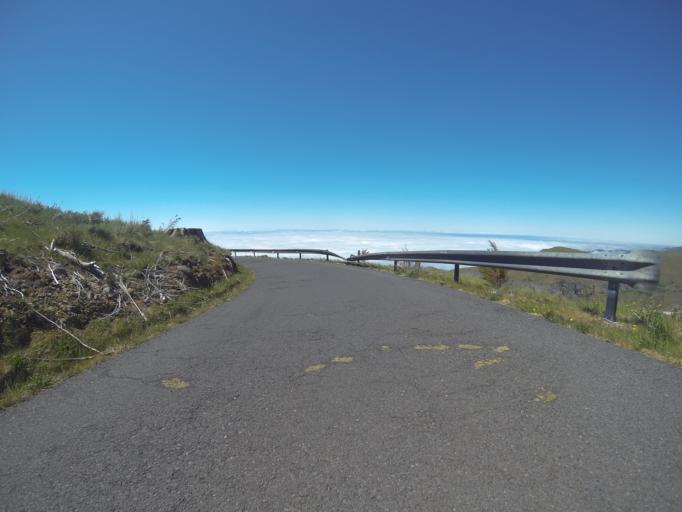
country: PT
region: Madeira
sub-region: Funchal
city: Nossa Senhora do Monte
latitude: 32.7074
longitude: -16.9152
